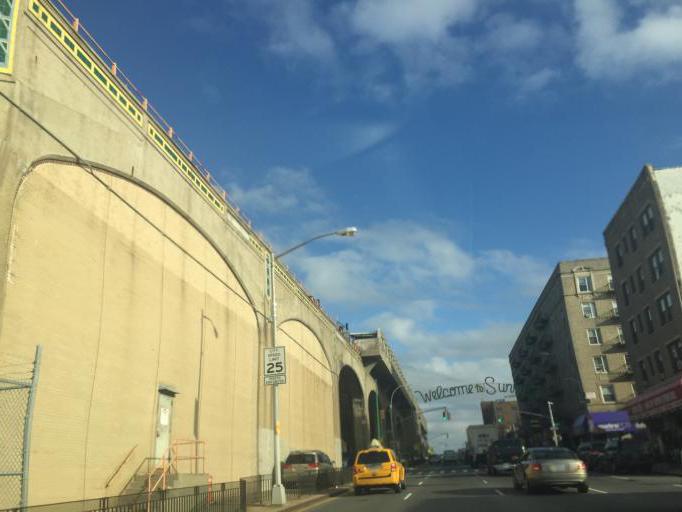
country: US
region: New York
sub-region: Queens County
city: Long Island City
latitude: 40.7439
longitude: -73.9259
